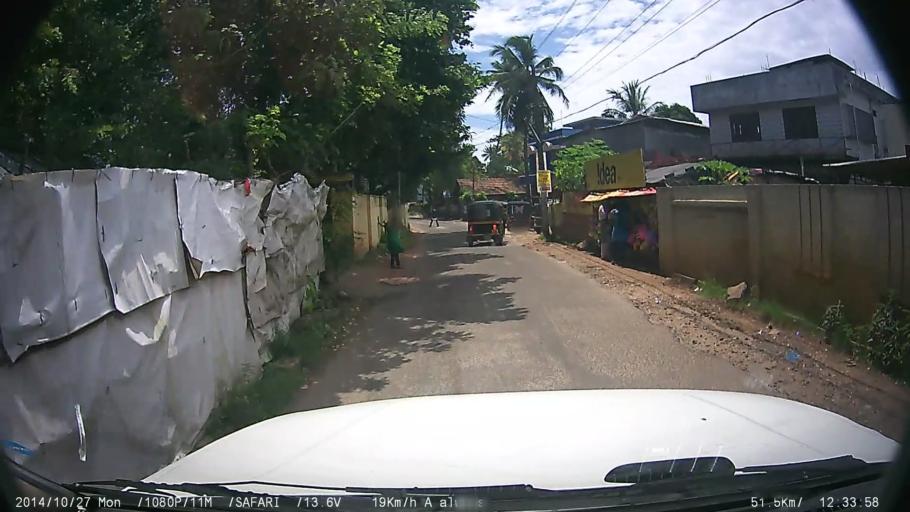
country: IN
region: Kerala
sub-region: Kottayam
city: Changanacheri
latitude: 9.4444
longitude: 76.5459
